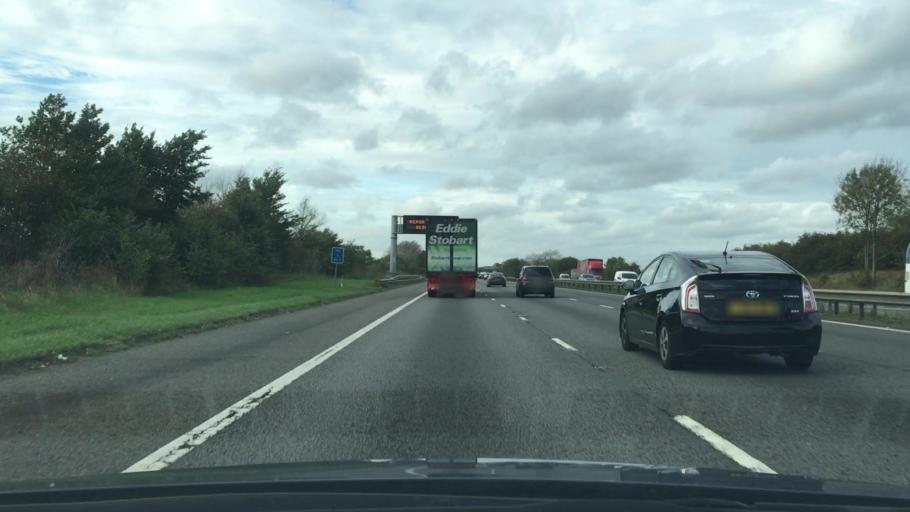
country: GB
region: England
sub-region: Milton Keynes
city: Hanslope
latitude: 52.1207
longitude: -0.8071
